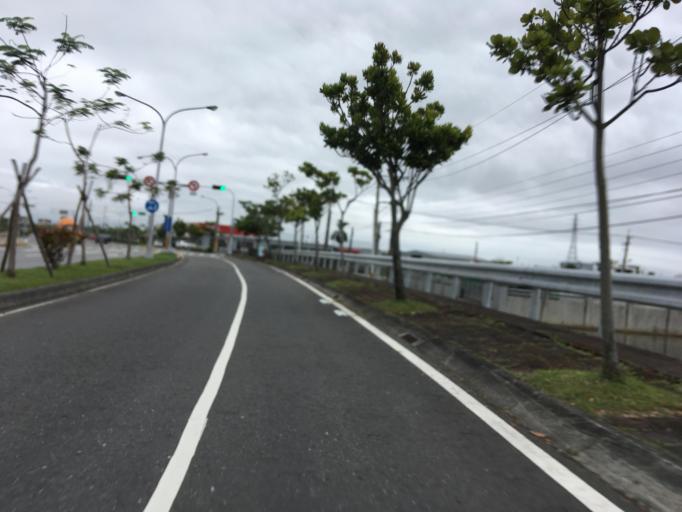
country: TW
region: Taiwan
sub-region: Yilan
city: Yilan
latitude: 24.7249
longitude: 121.7723
